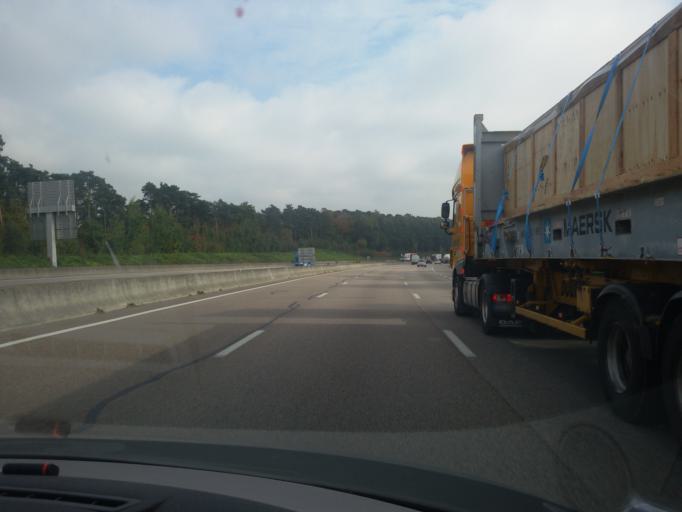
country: FR
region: Haute-Normandie
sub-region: Departement de la Seine-Maritime
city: Oissel
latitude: 49.3428
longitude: 1.0607
